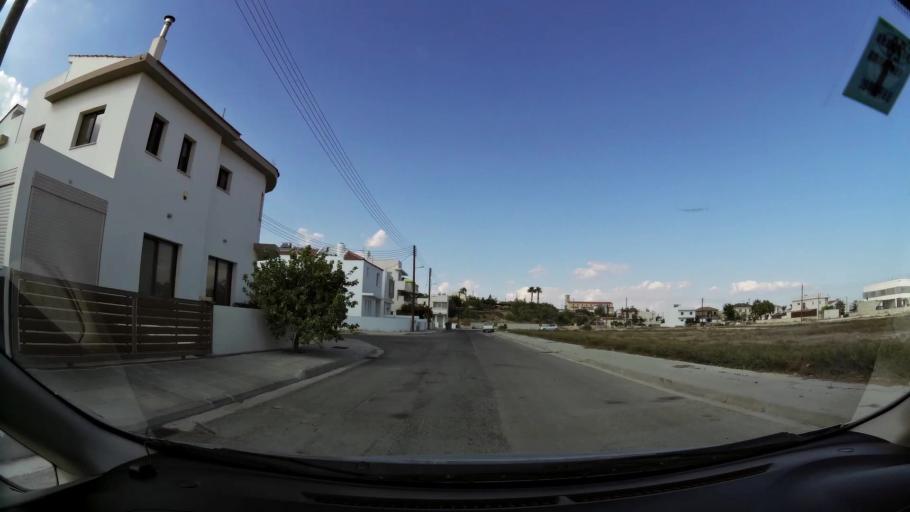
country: CY
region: Larnaka
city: Livadia
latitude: 34.9437
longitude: 33.6236
